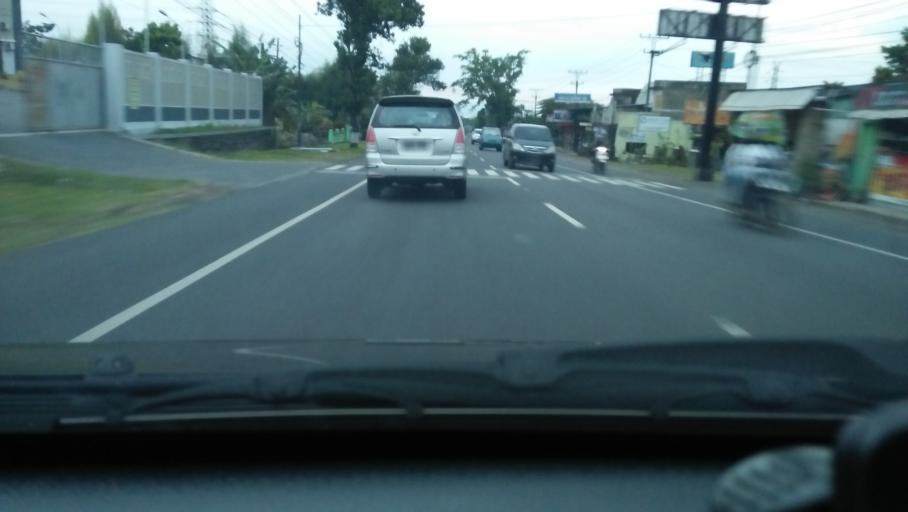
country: ID
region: Central Java
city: Magelang
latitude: -7.4140
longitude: 110.2356
